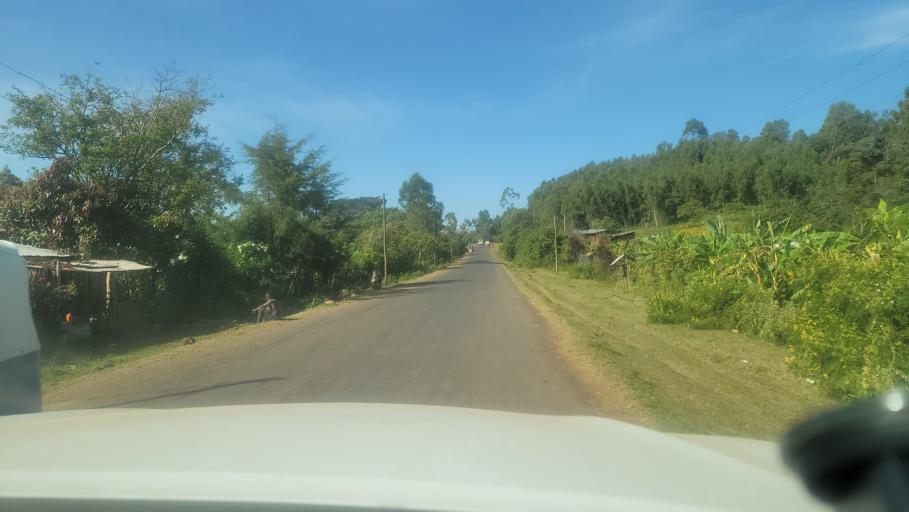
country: ET
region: Oromiya
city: Agaro
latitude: 7.7964
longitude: 36.4850
